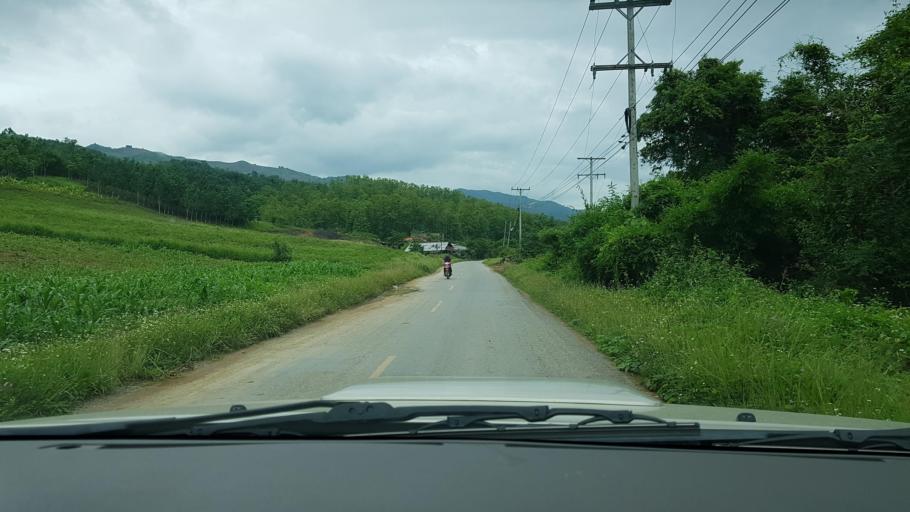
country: LA
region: Loungnamtha
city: Muang Nale
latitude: 20.2607
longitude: 101.5923
